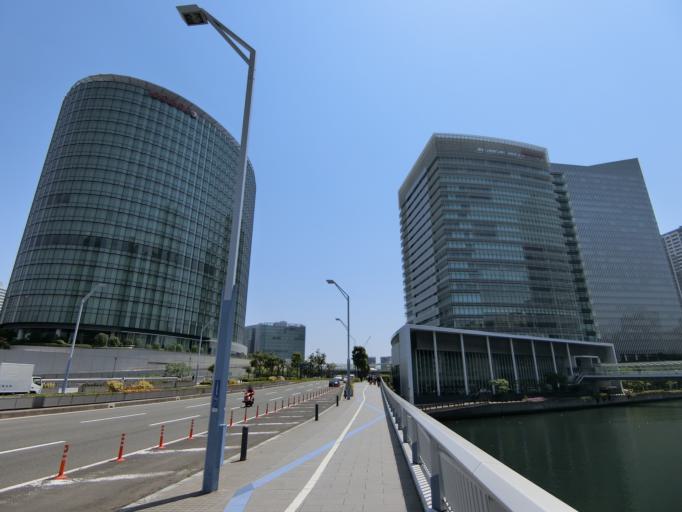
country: JP
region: Kanagawa
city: Yokohama
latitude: 35.4650
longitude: 139.6272
